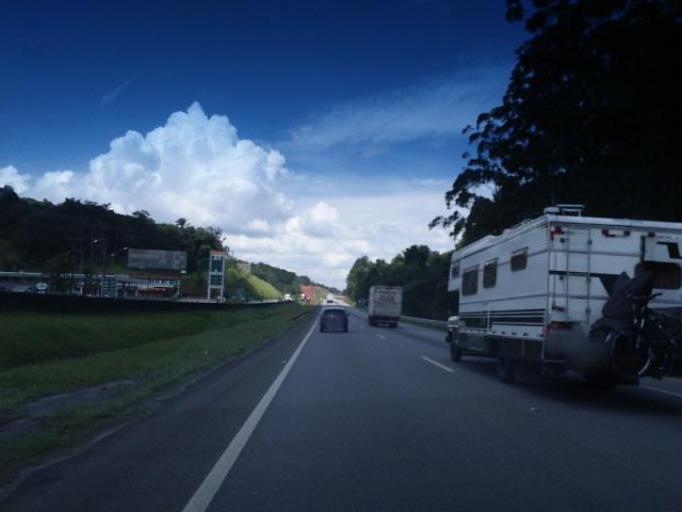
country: BR
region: Sao Paulo
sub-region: Juquitiba
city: Juquitiba
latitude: -23.9342
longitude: -47.0161
